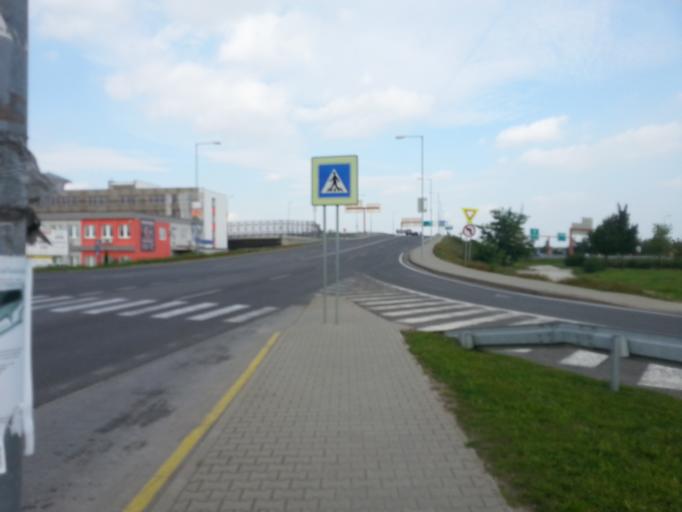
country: SK
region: Bratislavsky
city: Bratislava
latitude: 48.1698
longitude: 17.1834
